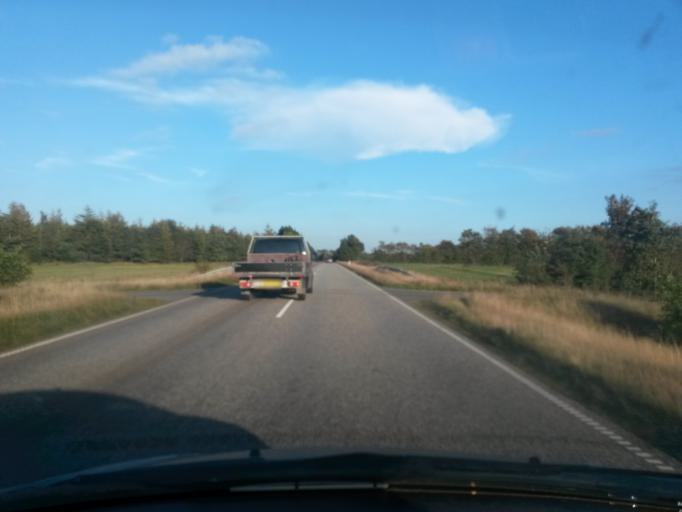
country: DK
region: Central Jutland
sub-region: Herning Kommune
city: Sunds
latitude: 56.3317
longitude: 8.9984
